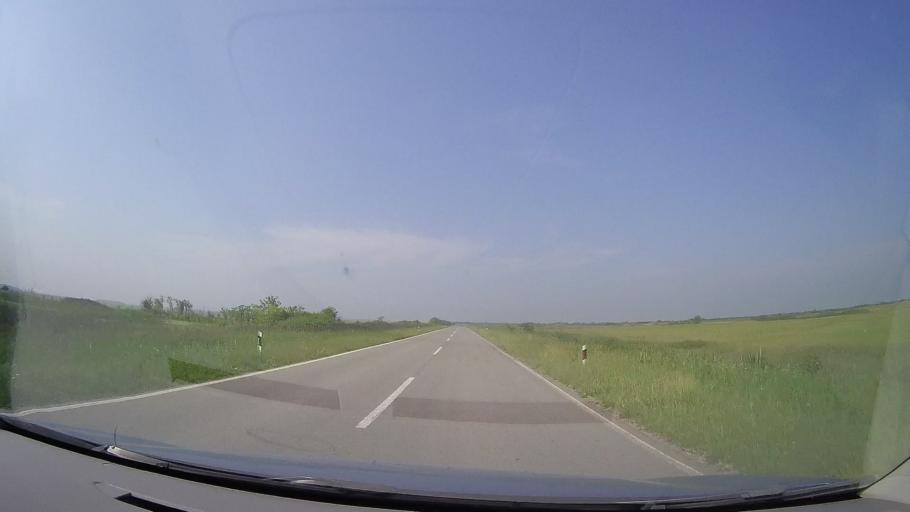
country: RS
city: Jasa Tomic
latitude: 45.4075
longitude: 20.8230
